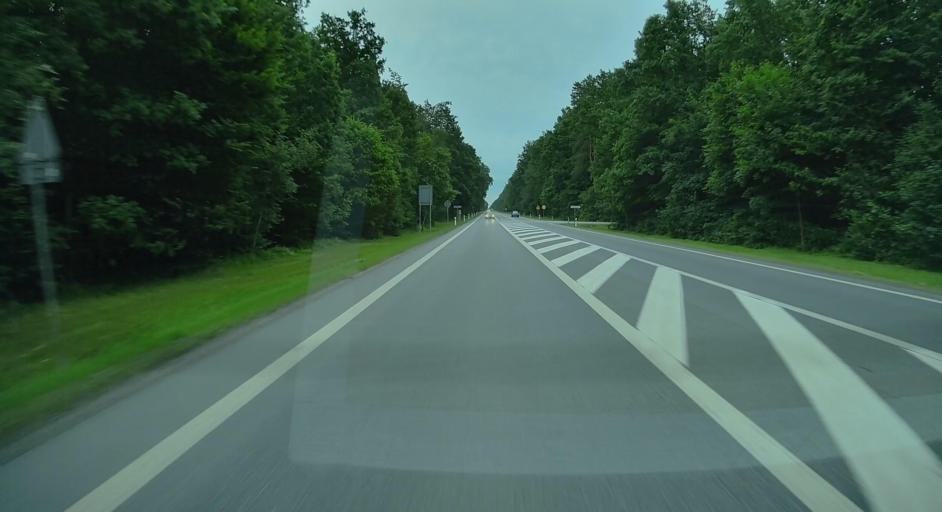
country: PL
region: Lublin Voivodeship
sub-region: Powiat bialski
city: Zalesie
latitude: 52.0358
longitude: 23.3920
